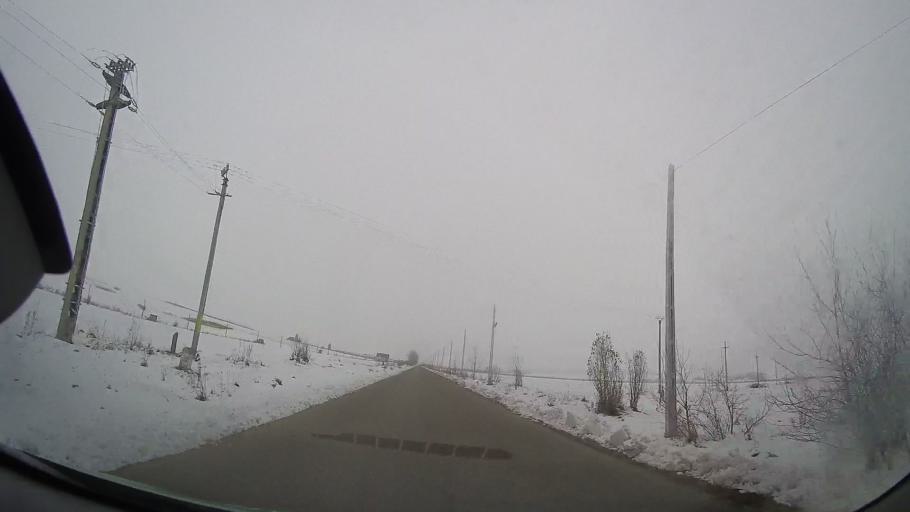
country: RO
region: Vaslui
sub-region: Comuna Todiresti
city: Todiresti
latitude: 46.8422
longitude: 27.3973
